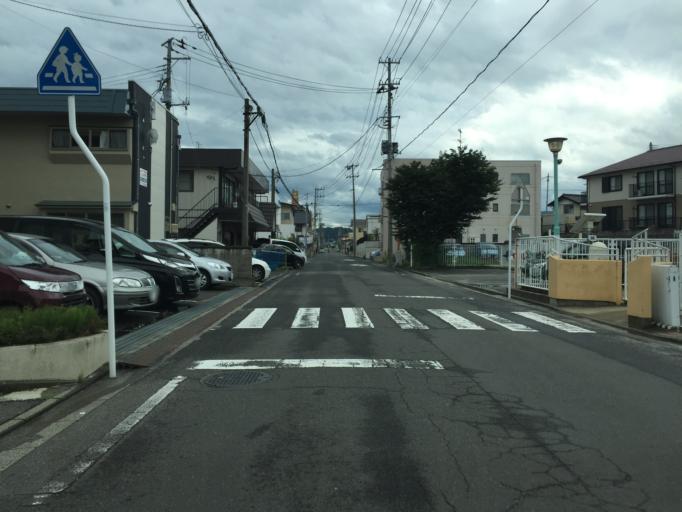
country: JP
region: Fukushima
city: Fukushima-shi
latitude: 37.7630
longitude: 140.4860
